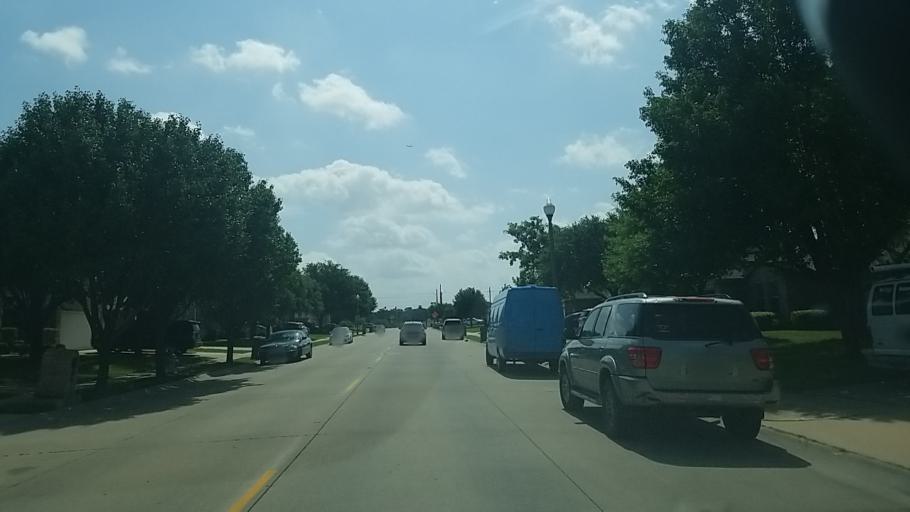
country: US
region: Texas
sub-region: Denton County
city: Corinth
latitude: 33.1419
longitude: -97.1078
